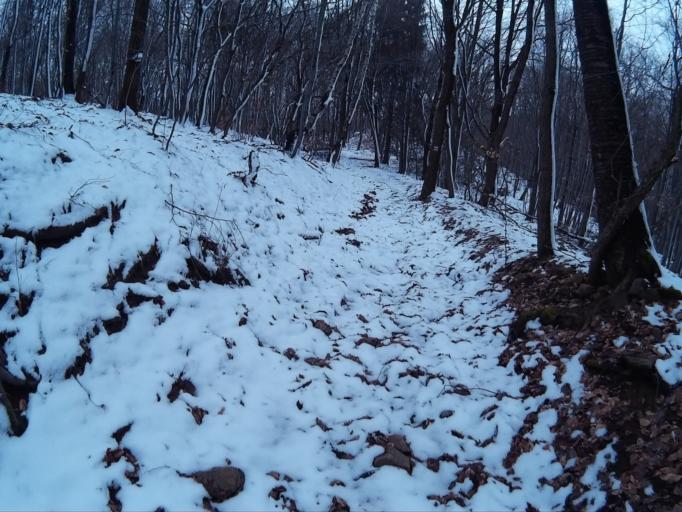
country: HU
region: Borsod-Abauj-Zemplen
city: Gonc
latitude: 48.4161
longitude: 21.3554
